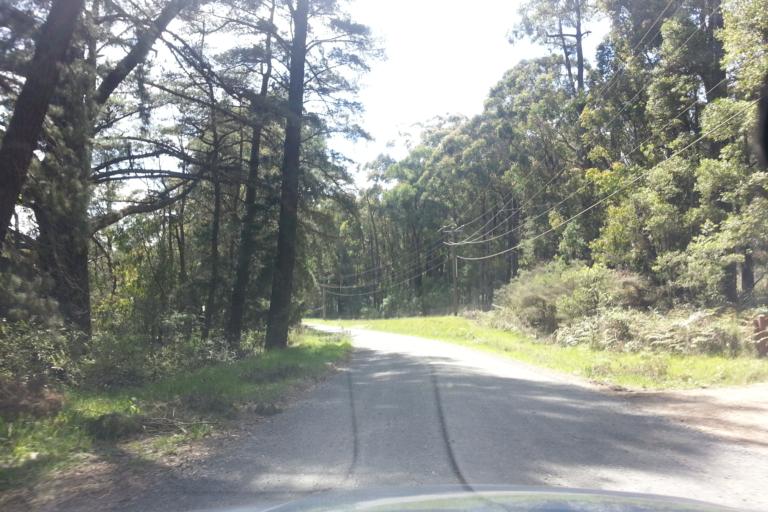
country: AU
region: Victoria
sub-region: Cardinia
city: Gembrook
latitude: -37.9540
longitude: 145.5690
